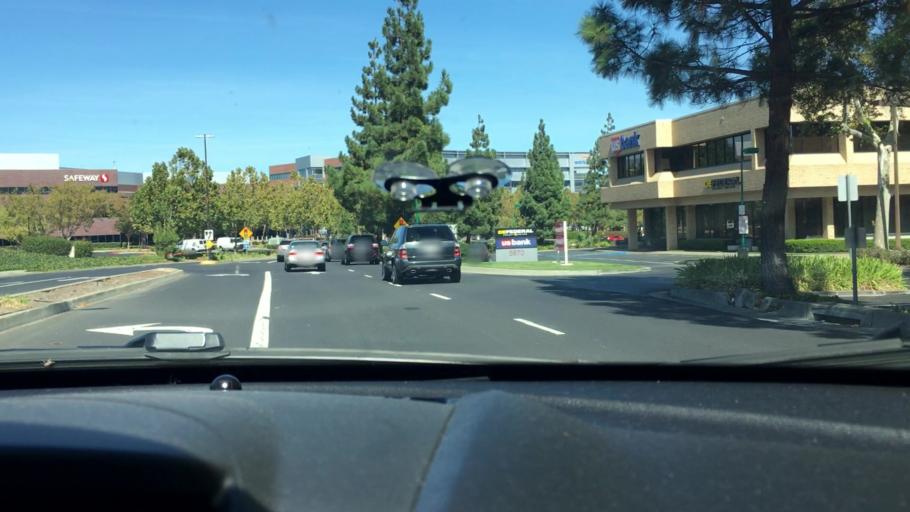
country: US
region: California
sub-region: Alameda County
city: Dublin
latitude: 37.6953
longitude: -121.9329
